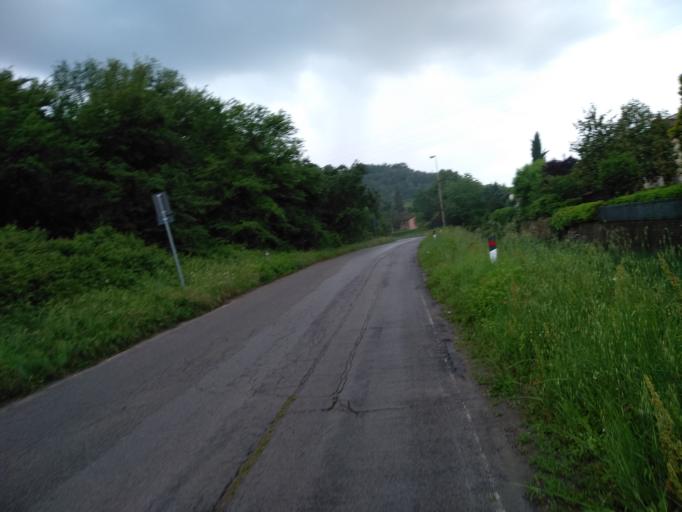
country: IT
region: Tuscany
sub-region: Province of Arezzo
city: San Giovanni Valdarno
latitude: 43.5589
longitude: 11.5254
